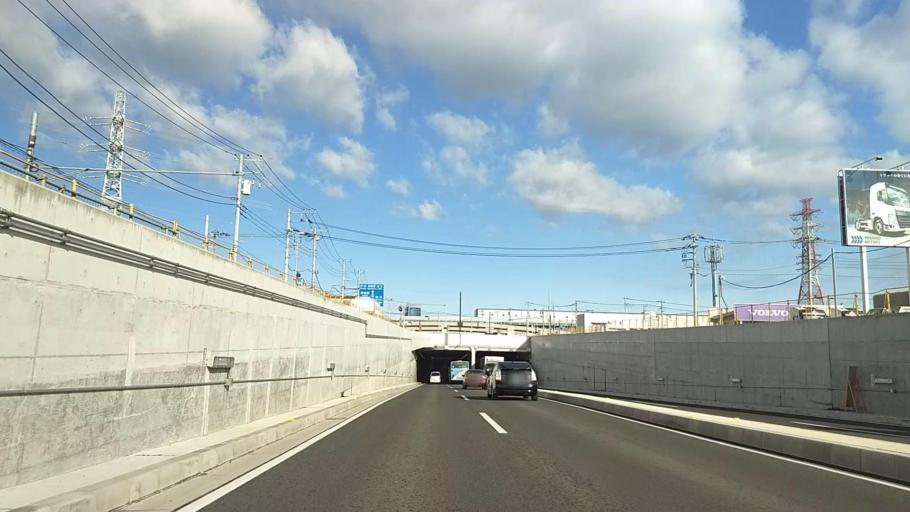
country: JP
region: Kanagawa
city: Atsugi
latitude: 35.4033
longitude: 139.3616
